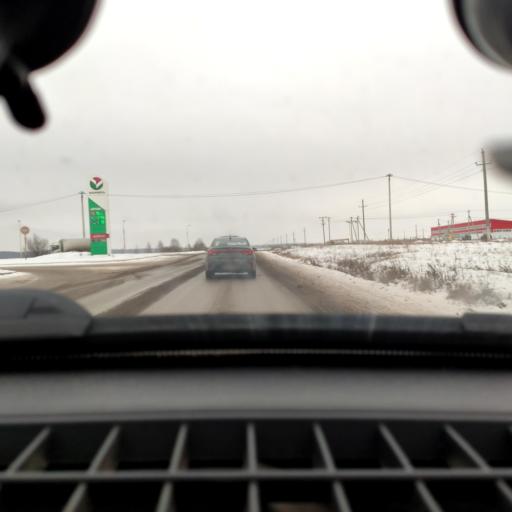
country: RU
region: Bashkortostan
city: Iglino
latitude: 54.8020
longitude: 56.4131
